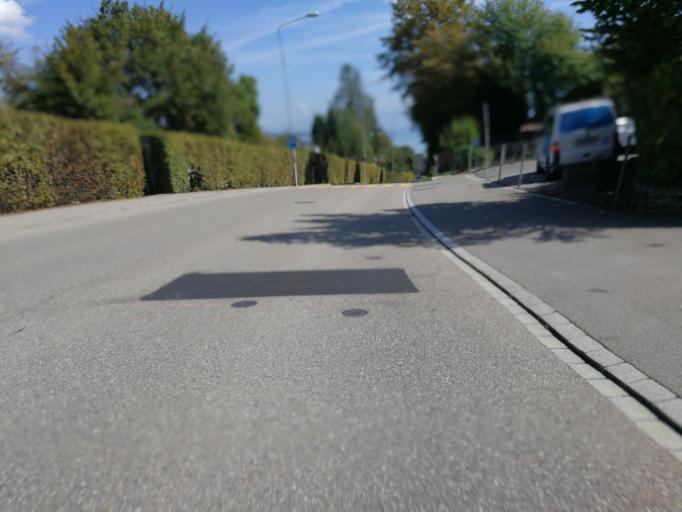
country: CH
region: Zurich
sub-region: Bezirk Horgen
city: Au / Mittel-Dorf
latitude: 47.2419
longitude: 8.6463
